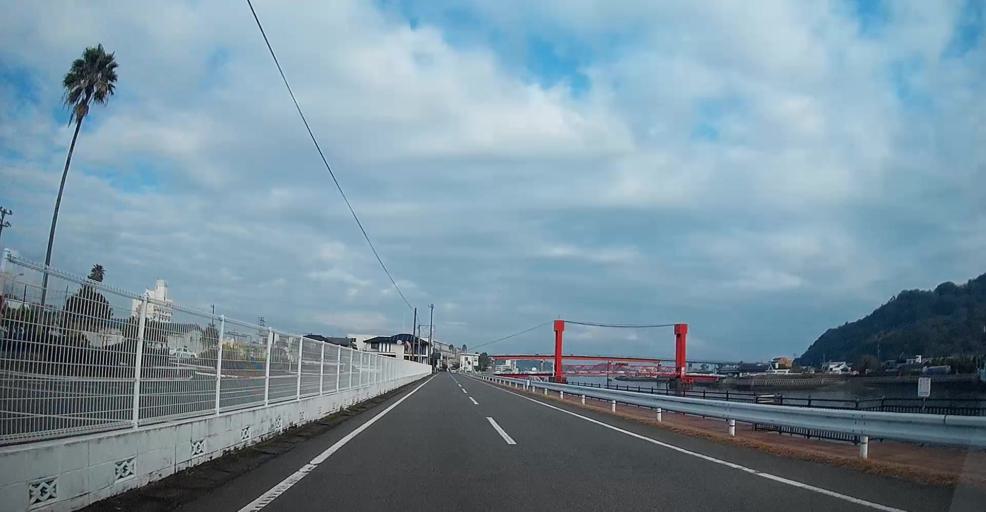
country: JP
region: Kumamoto
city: Hondo
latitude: 32.4435
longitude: 130.2041
